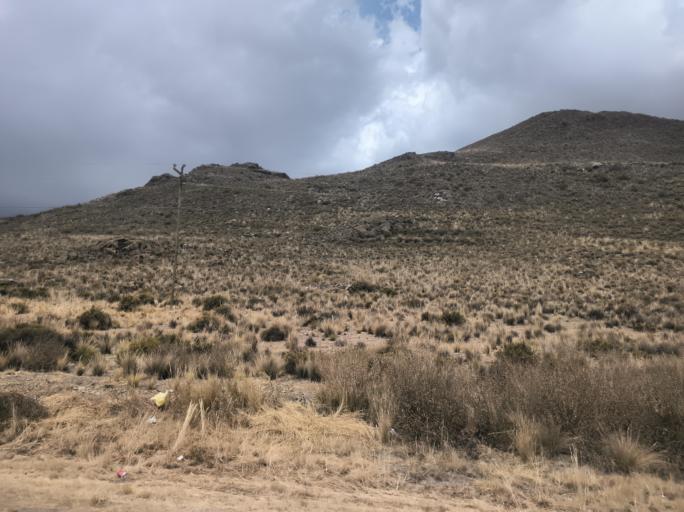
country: BO
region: Oruro
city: Challapata
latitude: -18.7618
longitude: -66.8608
